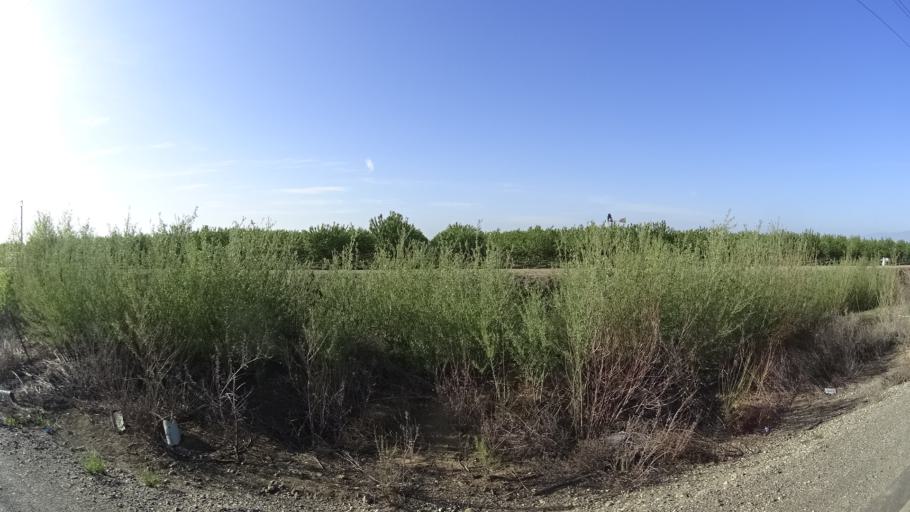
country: US
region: California
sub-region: Glenn County
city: Willows
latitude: 39.5824
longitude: -122.2404
